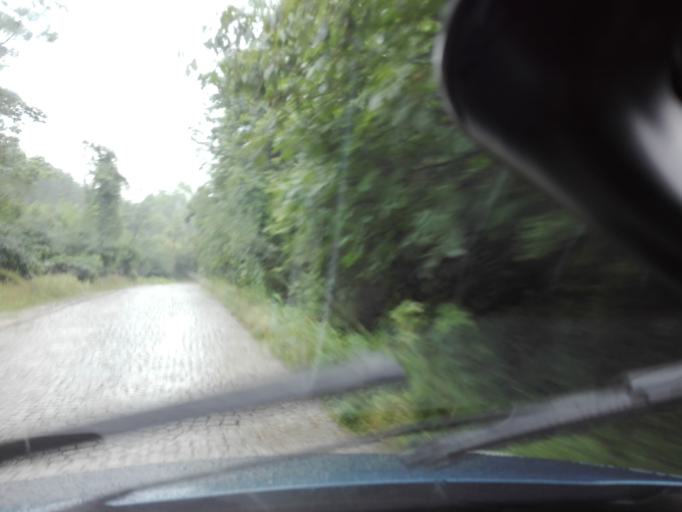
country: BG
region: Sofia-Capital
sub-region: Stolichna Obshtina
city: Sofia
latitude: 42.6060
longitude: 23.3942
